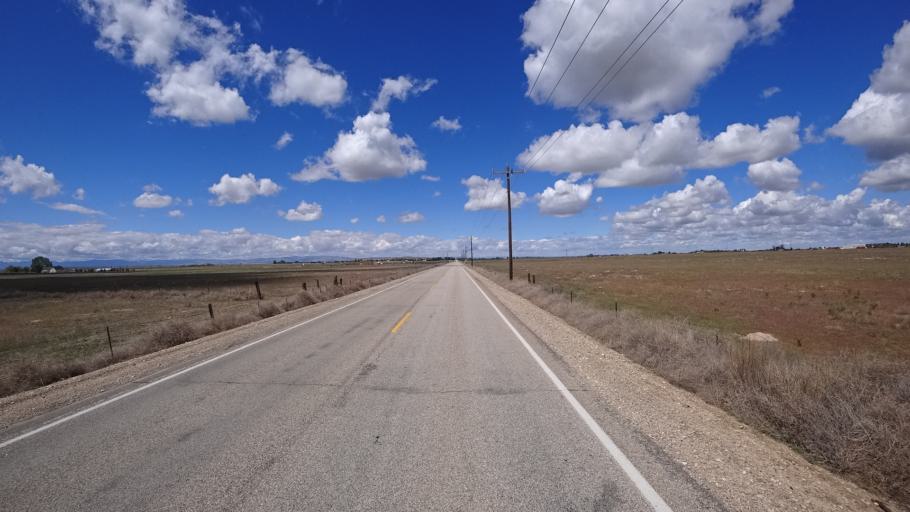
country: US
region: Idaho
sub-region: Ada County
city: Kuna
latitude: 43.4592
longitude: -116.3090
